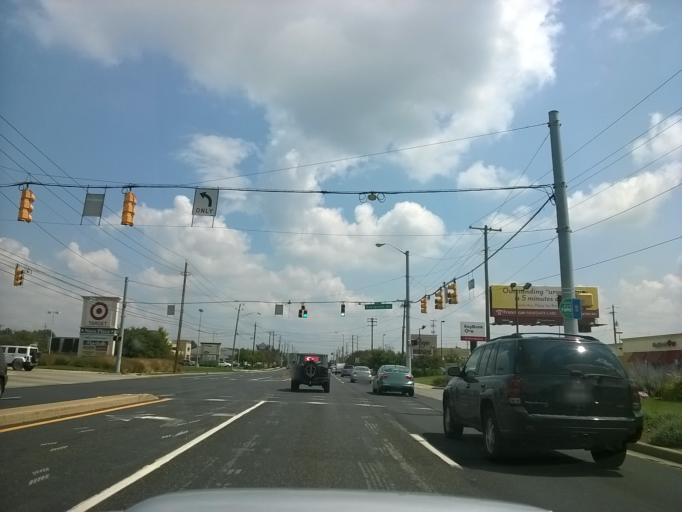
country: US
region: Indiana
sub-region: Marion County
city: Meridian Hills
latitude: 39.9125
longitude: -86.1389
